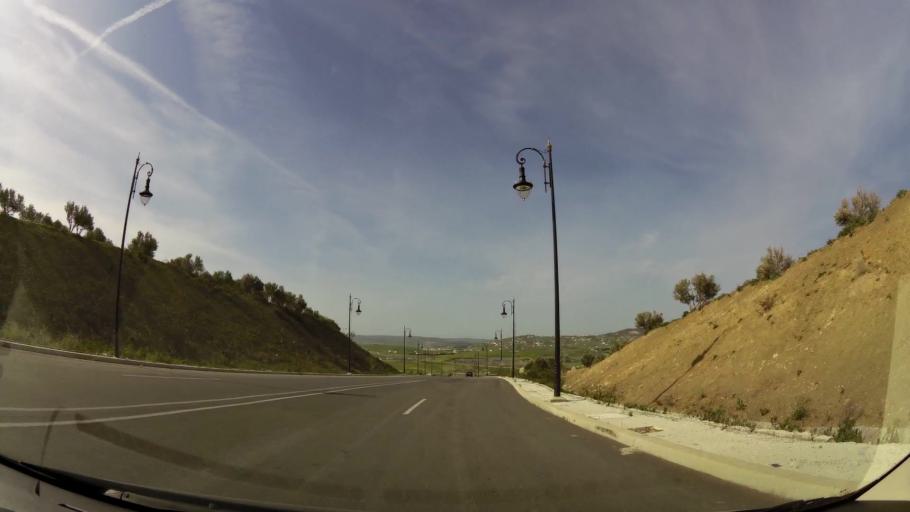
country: MA
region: Tanger-Tetouan
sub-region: Tanger-Assilah
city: Tangier
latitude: 35.7037
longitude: -5.7941
